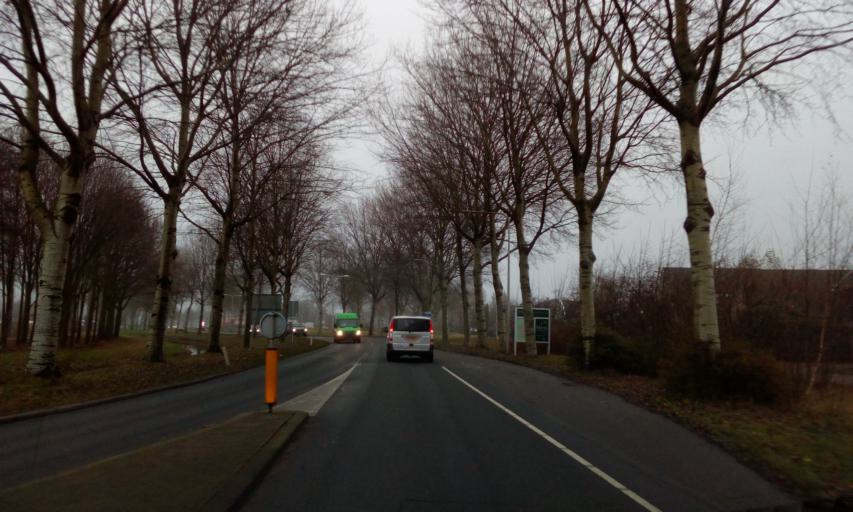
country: NL
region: South Holland
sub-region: Gemeente Capelle aan den IJssel
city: Capelle aan den IJssel
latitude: 51.9653
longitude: 4.5961
